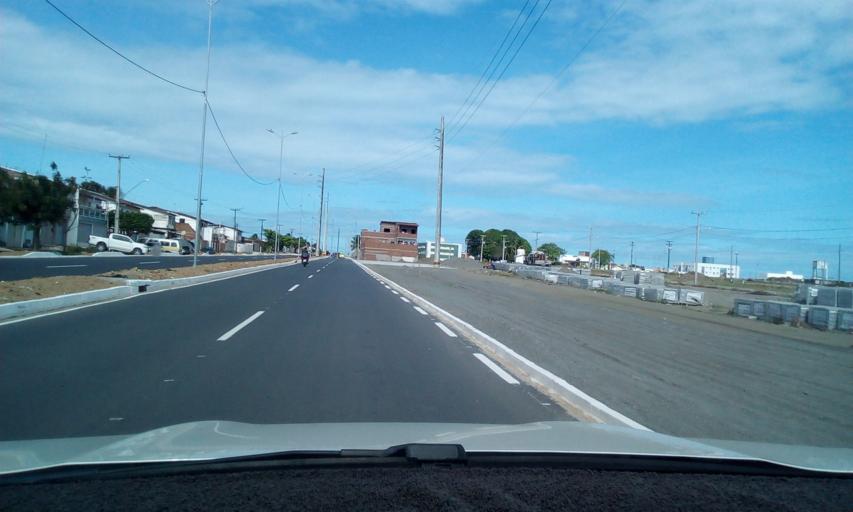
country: BR
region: Paraiba
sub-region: Conde
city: Conde
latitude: -7.2080
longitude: -34.8465
